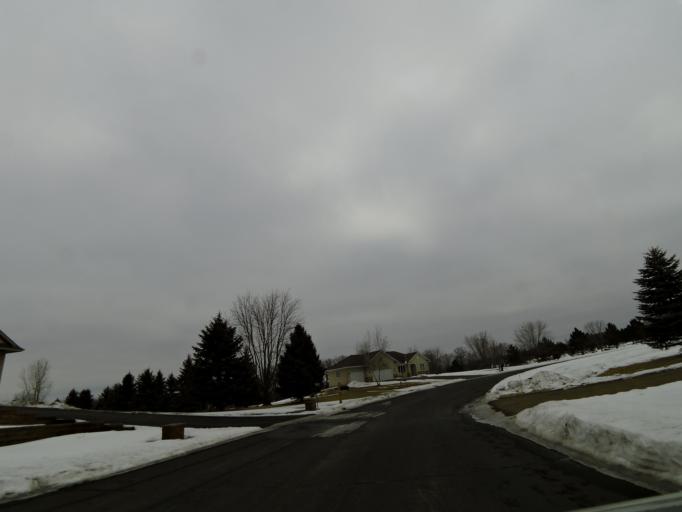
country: US
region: Minnesota
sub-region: Washington County
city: Afton
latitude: 44.8500
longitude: -92.7950
